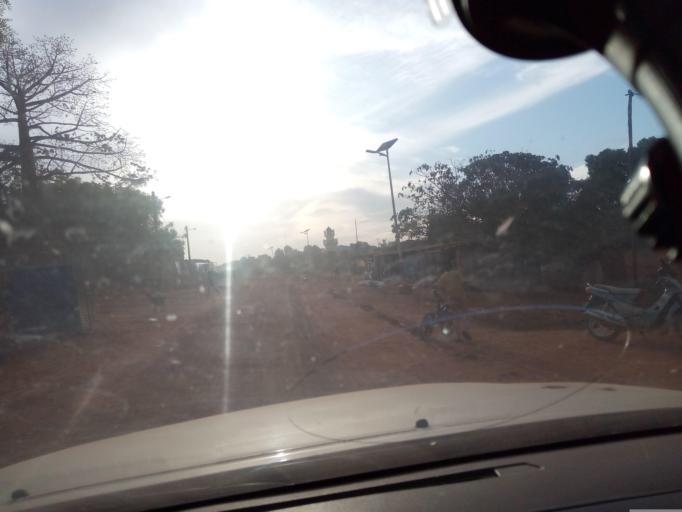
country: ML
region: Sikasso
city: Sikasso
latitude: 11.3124
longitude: -5.6514
